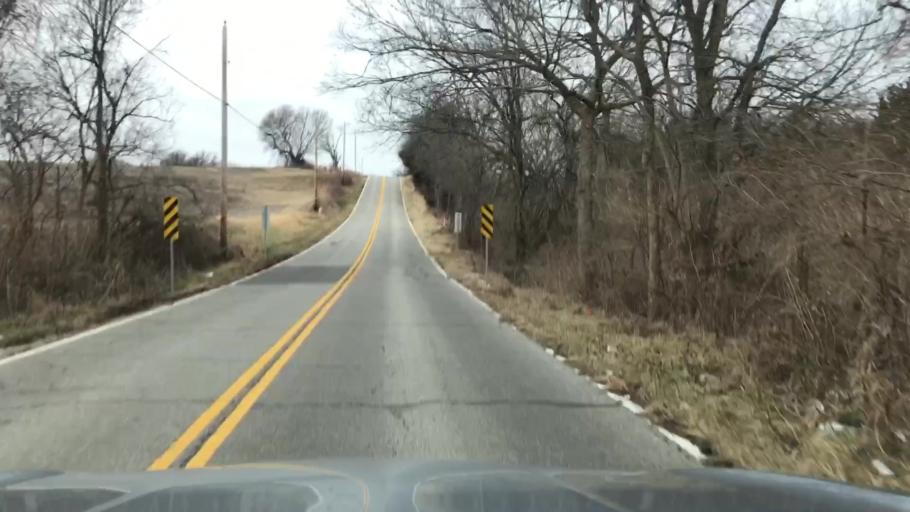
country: US
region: Missouri
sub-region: Jackson County
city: Lees Summit
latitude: 38.8897
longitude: -94.4038
